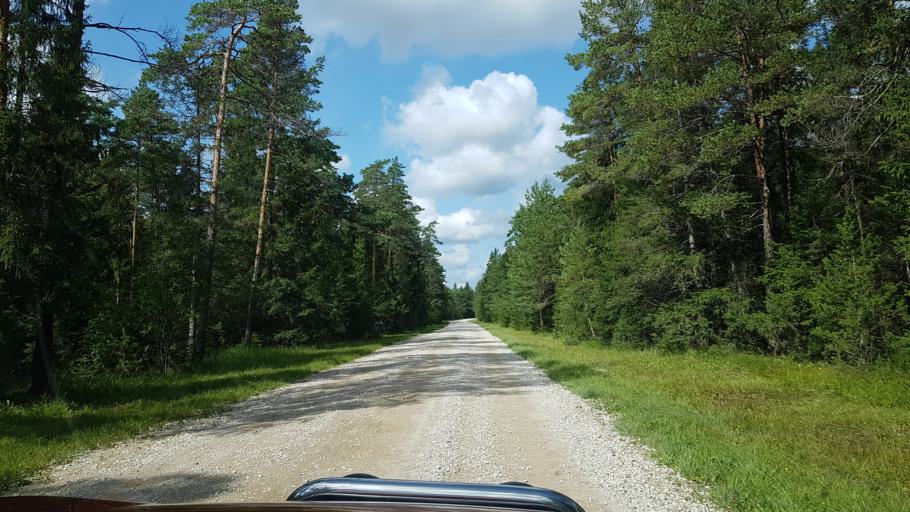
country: EE
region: Raplamaa
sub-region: Rapla vald
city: Rapla
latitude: 58.9619
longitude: 24.6435
